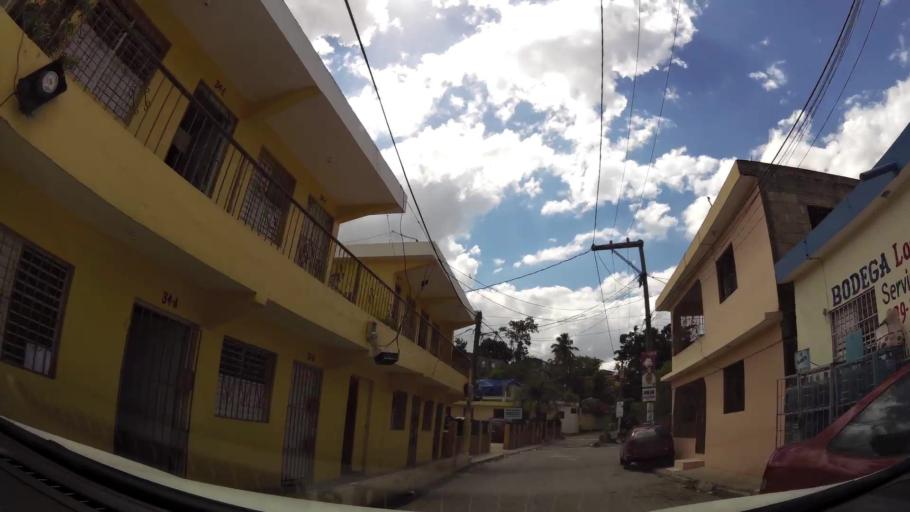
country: DO
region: Nacional
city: Ensanche Luperon
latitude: 18.5296
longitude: -69.9111
